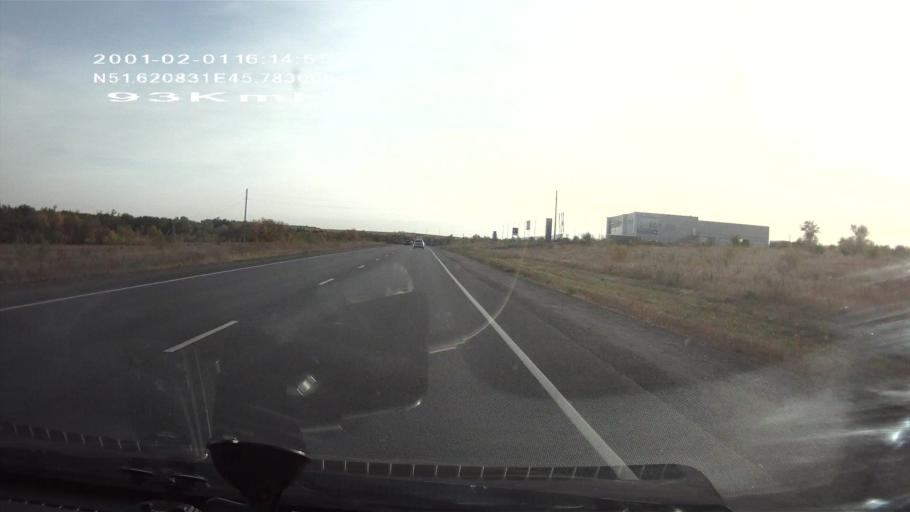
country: RU
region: Saratov
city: Sokolovyy
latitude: 51.6207
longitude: 45.7827
